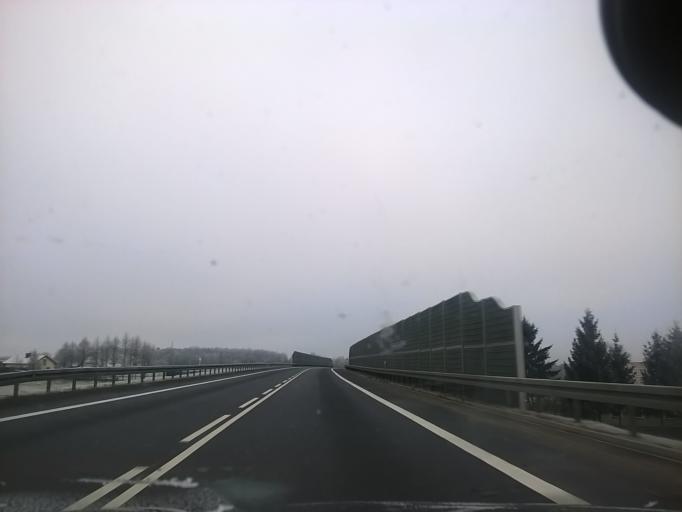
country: PL
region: Warmian-Masurian Voivodeship
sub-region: Powiat olsztynski
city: Biskupiec
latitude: 53.8374
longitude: 20.9291
